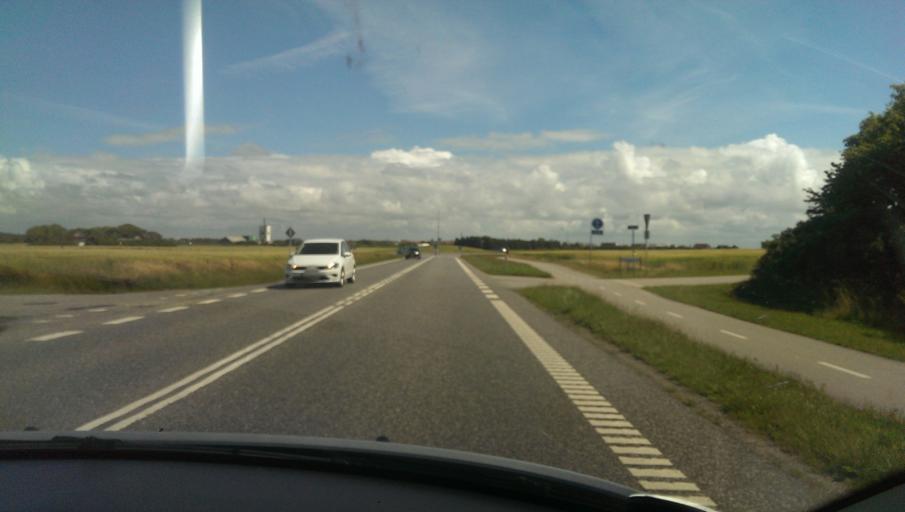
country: DK
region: Central Jutland
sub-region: Ringkobing-Skjern Kommune
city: Ringkobing
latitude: 56.1017
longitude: 8.2193
